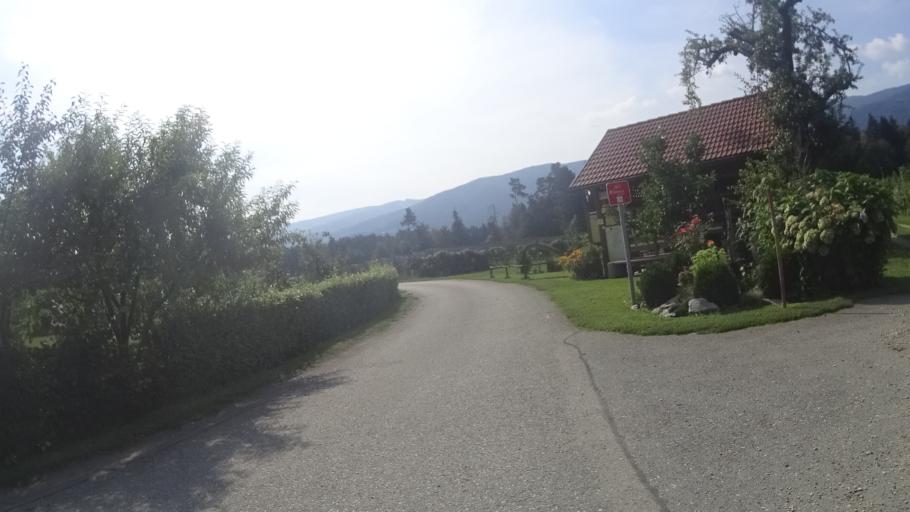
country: SI
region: Selnica ob Dravi
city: Selnica ob Dravi
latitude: 46.5441
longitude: 15.4825
